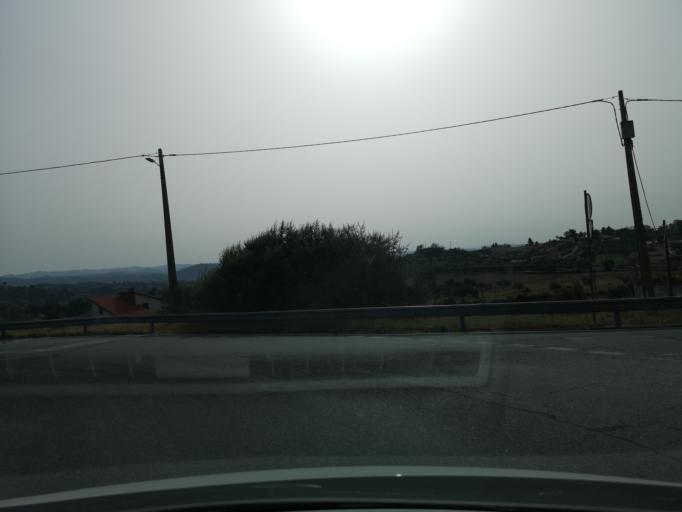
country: PT
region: Castelo Branco
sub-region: Belmonte
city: Belmonte
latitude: 40.3465
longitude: -7.3486
